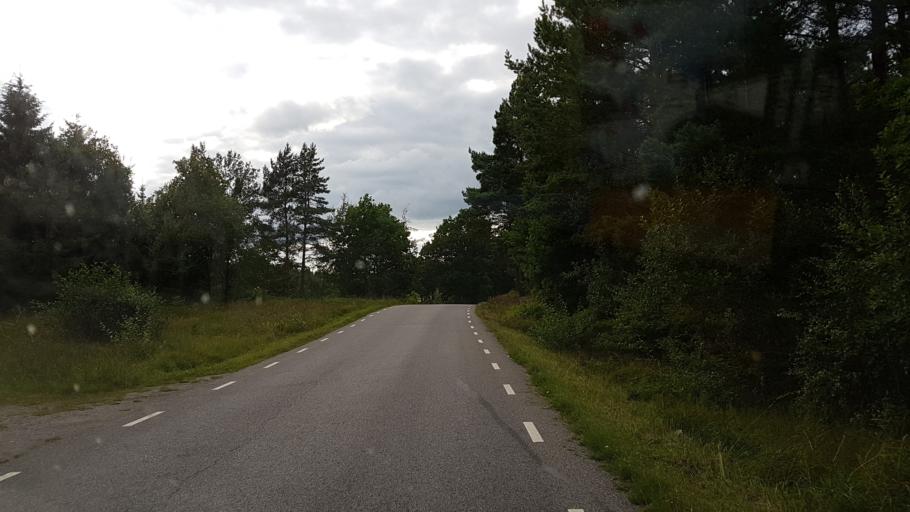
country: SE
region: OEstergoetland
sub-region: Valdemarsviks Kommun
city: Gusum
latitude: 58.4570
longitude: 16.5903
